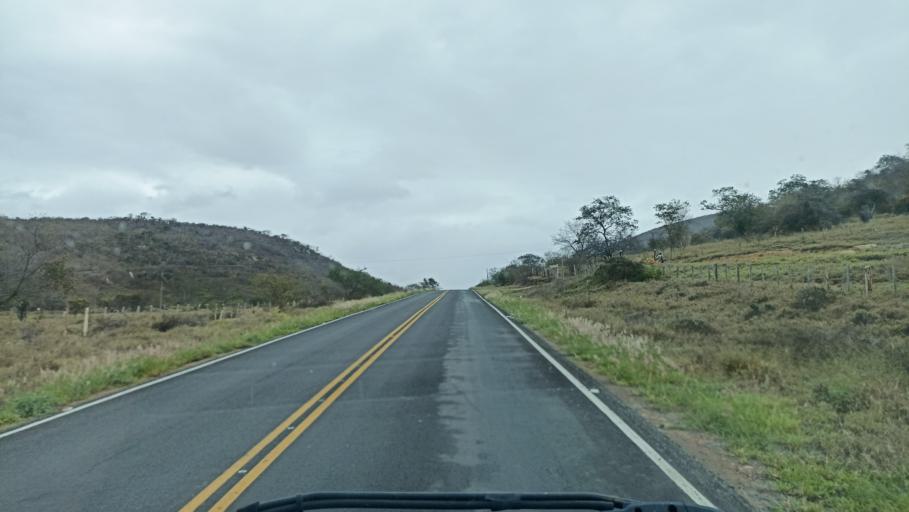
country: BR
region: Bahia
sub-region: Andarai
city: Vera Cruz
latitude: -13.0463
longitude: -40.7759
